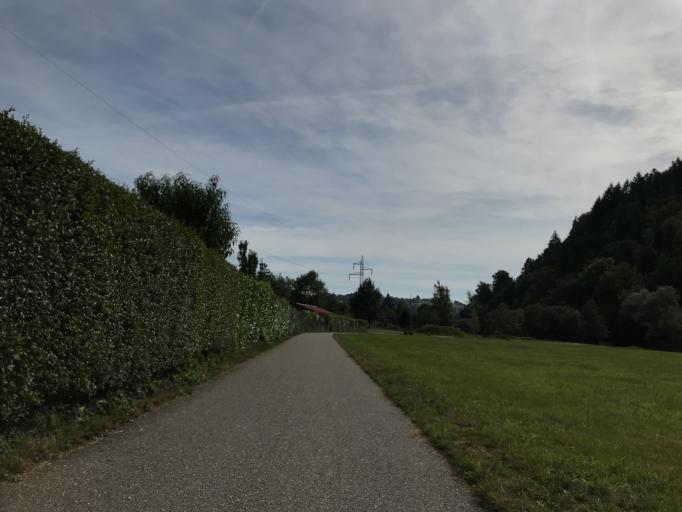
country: DE
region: Baden-Wuerttemberg
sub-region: Freiburg Region
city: Schopfheim
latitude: 47.6599
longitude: 7.8297
